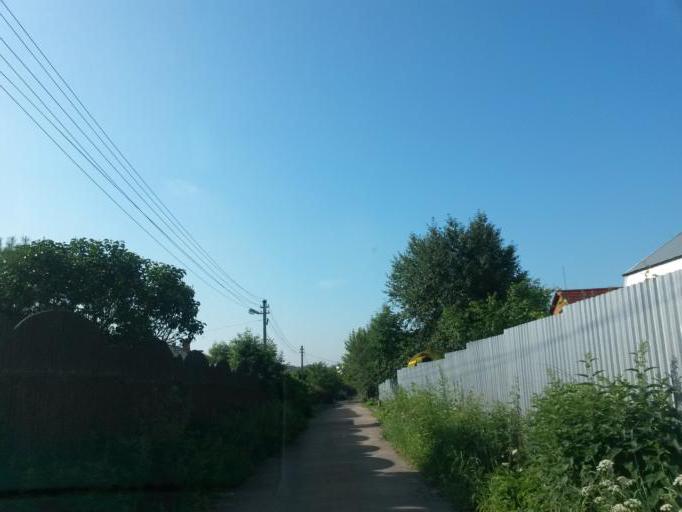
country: RU
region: Moscow
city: Zyablikovo
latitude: 55.5900
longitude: 37.7680
